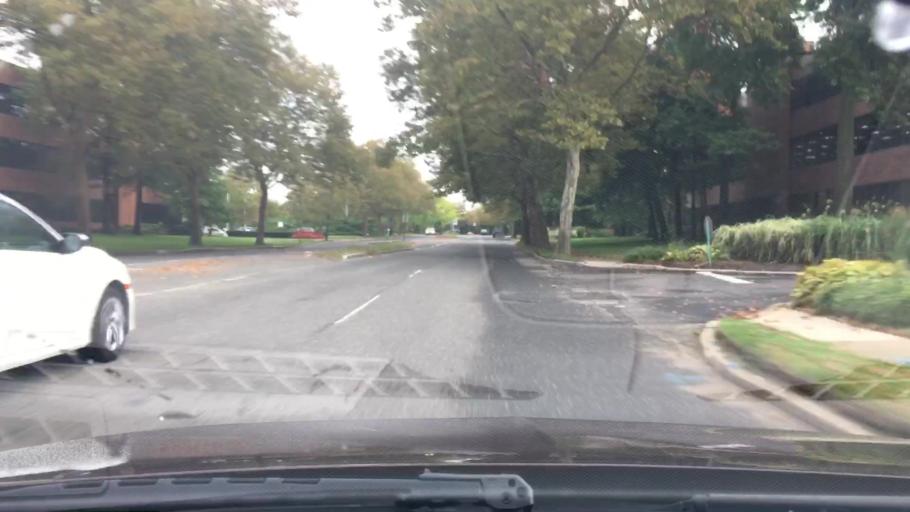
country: US
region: New York
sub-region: Suffolk County
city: Melville
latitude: 40.7682
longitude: -73.4152
